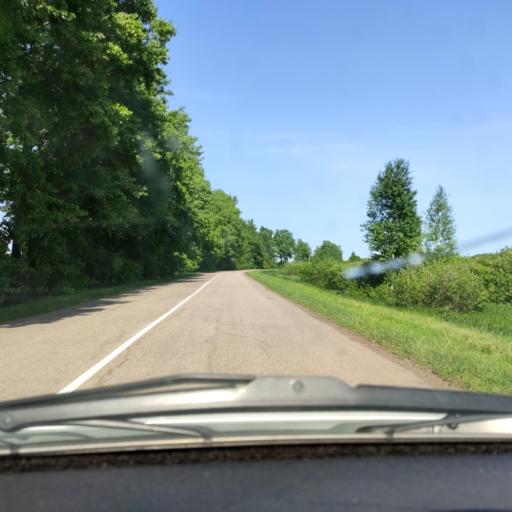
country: RU
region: Bashkortostan
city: Chishmy
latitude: 54.4830
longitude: 55.5730
